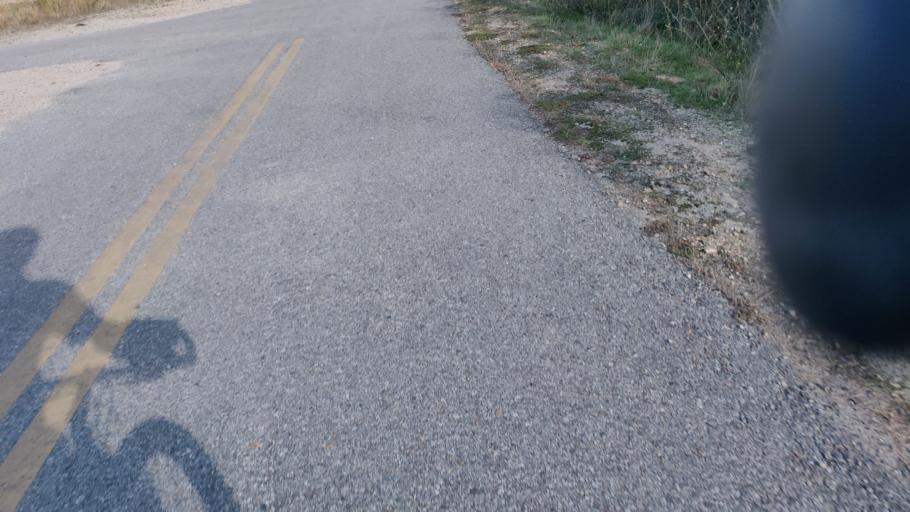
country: US
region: Idaho
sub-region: Ada County
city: Boise
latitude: 43.5717
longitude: -116.1374
